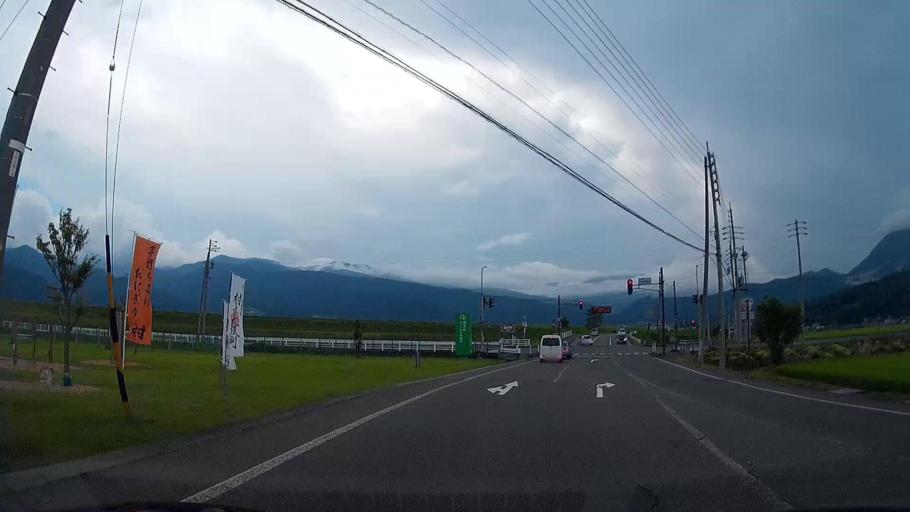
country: JP
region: Nagano
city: Iiyama
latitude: 36.8518
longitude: 138.3886
